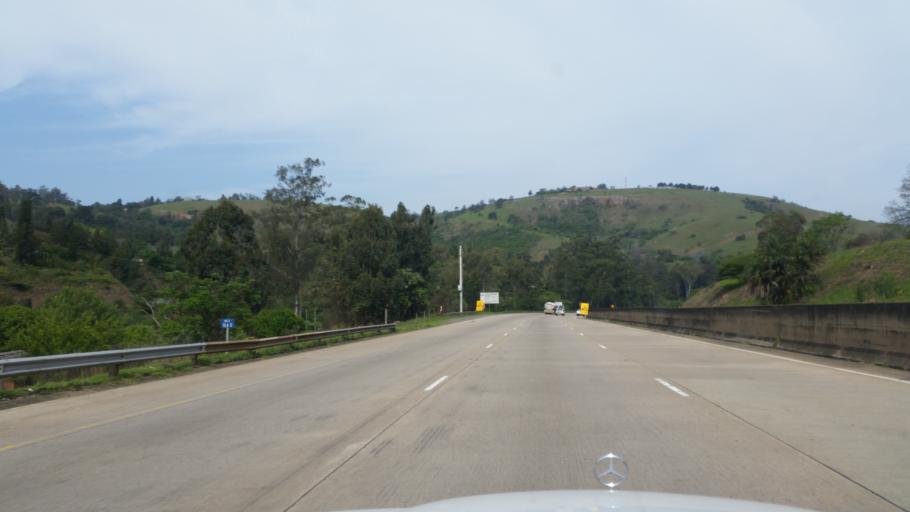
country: ZA
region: KwaZulu-Natal
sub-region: eThekwini Metropolitan Municipality
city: Mpumalanga
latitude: -29.7401
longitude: 30.6579
